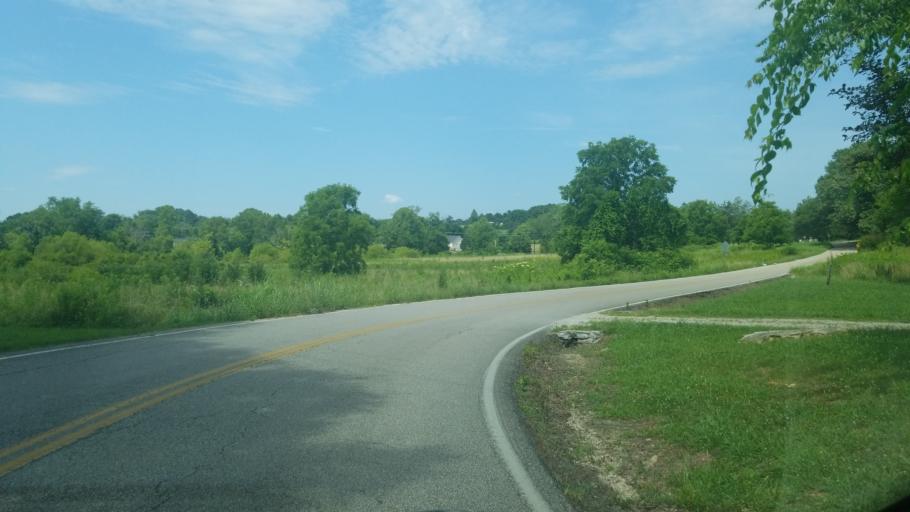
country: US
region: Tennessee
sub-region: Hamilton County
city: Lakesite
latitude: 35.1825
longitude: -85.0398
